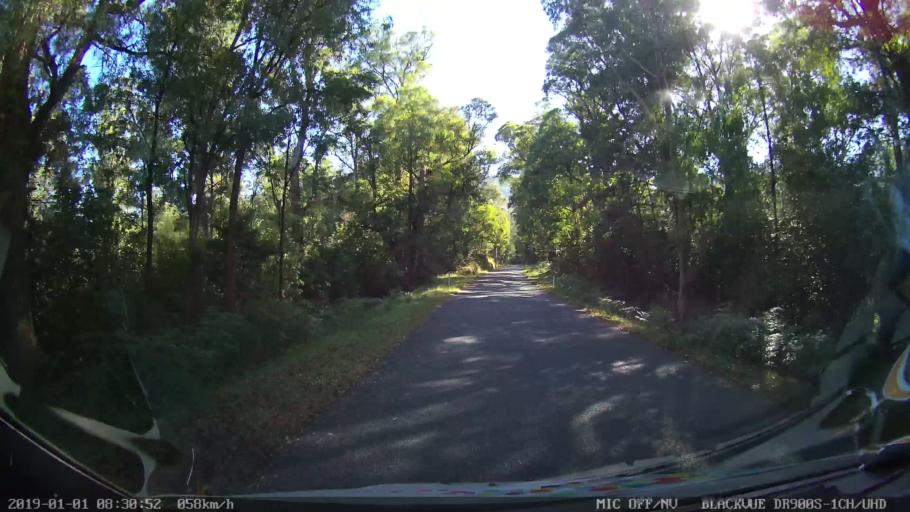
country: AU
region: New South Wales
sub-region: Snowy River
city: Jindabyne
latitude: -36.3731
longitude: 148.2009
